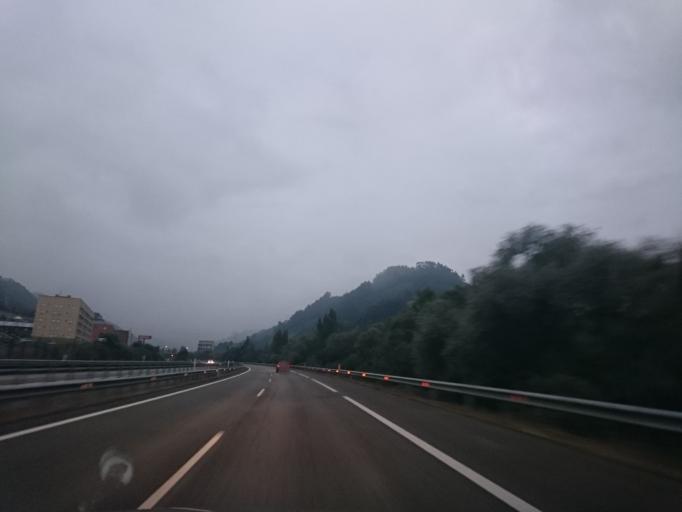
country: ES
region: Asturias
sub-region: Province of Asturias
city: Mieres
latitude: 43.2289
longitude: -5.7829
